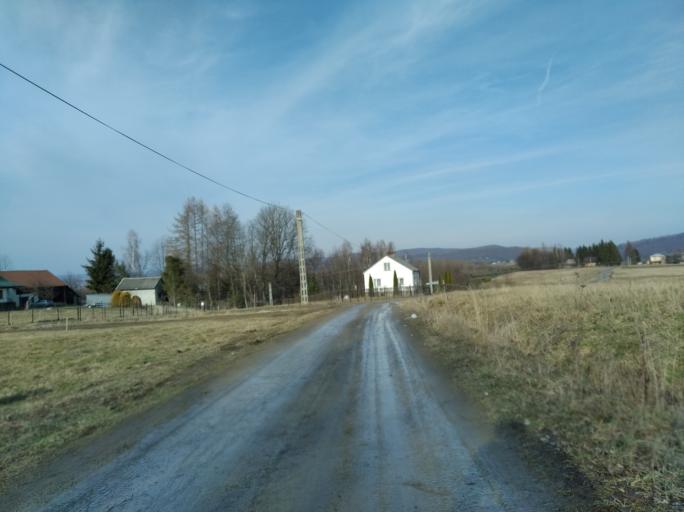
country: PL
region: Subcarpathian Voivodeship
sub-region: Powiat brzozowski
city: Gorki
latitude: 49.6463
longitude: 22.0585
